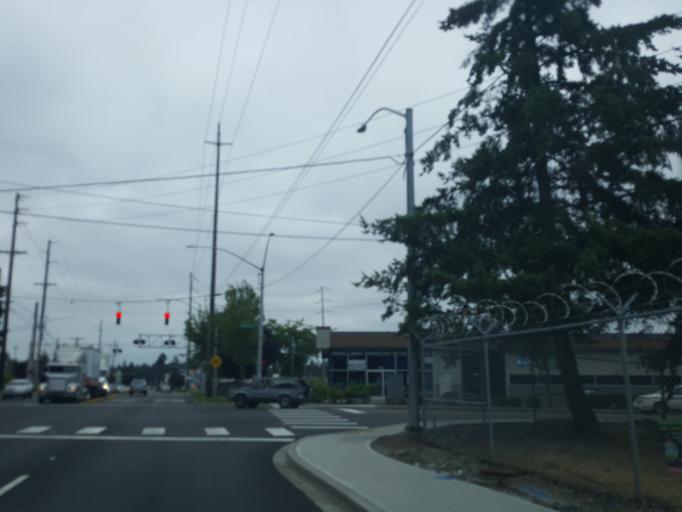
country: US
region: Washington
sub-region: Pierce County
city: Lakewood
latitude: 47.1765
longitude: -122.4915
